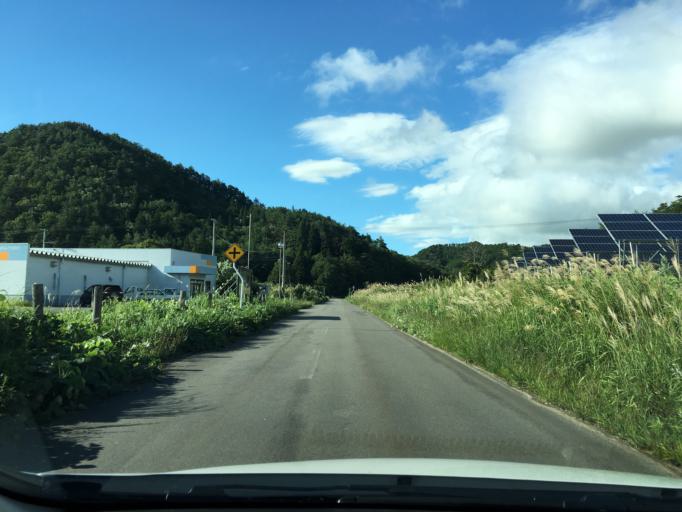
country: JP
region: Yamagata
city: Yonezawa
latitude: 37.8864
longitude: 140.1927
